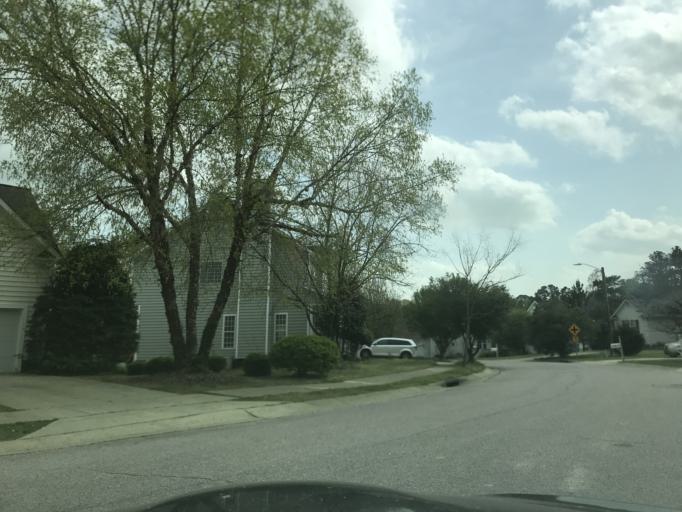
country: US
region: North Carolina
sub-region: Wake County
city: Raleigh
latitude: 35.8219
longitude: -78.5833
